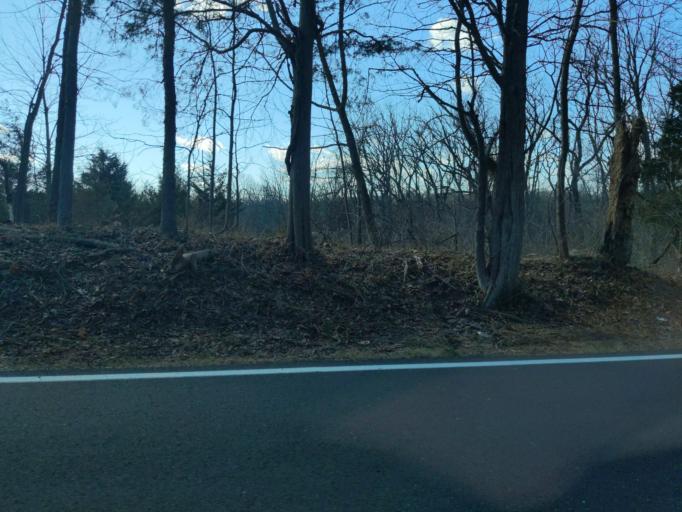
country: US
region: Pennsylvania
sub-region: Montgomery County
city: Red Hill
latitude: 40.3645
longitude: -75.4563
